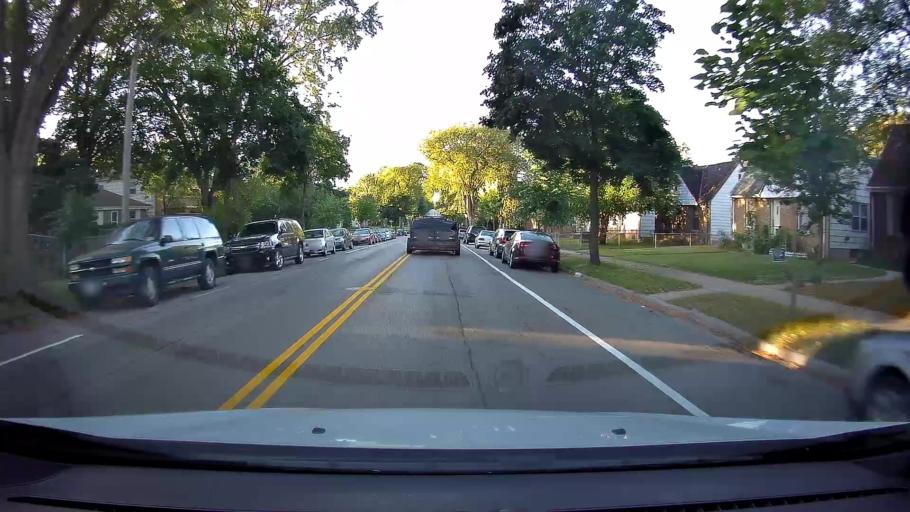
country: US
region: Minnesota
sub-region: Hennepin County
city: Richfield
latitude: 44.9246
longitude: -93.2474
